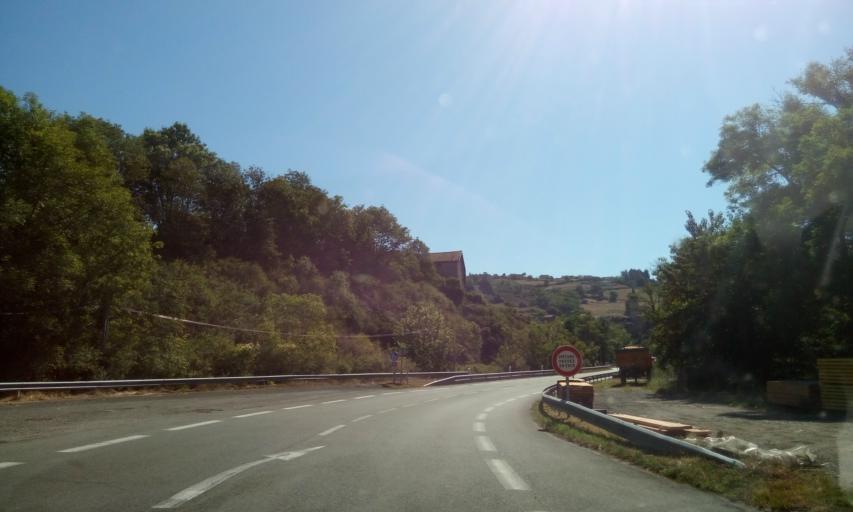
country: FR
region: Rhone-Alpes
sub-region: Departement du Rhone
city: Grandris
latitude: 45.9870
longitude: 4.5047
